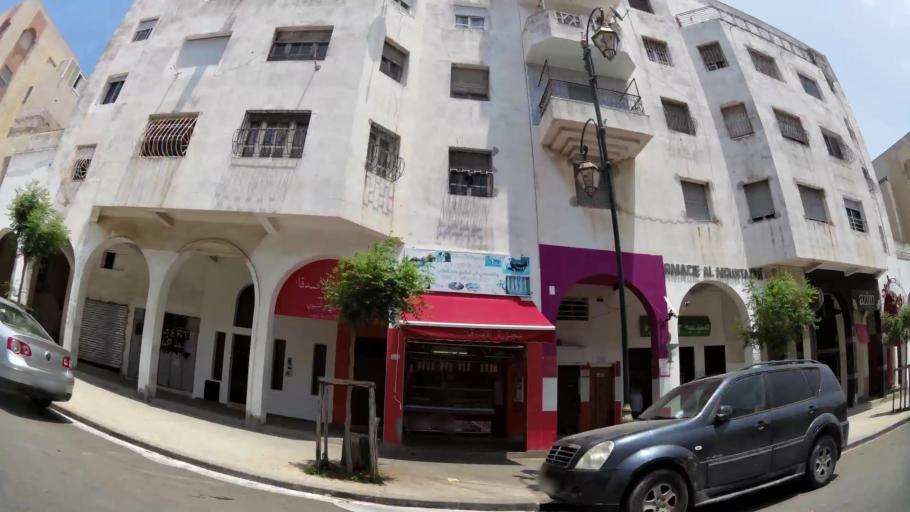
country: MA
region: Rabat-Sale-Zemmour-Zaer
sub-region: Skhirate-Temara
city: Temara
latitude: 33.9686
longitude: -6.8980
